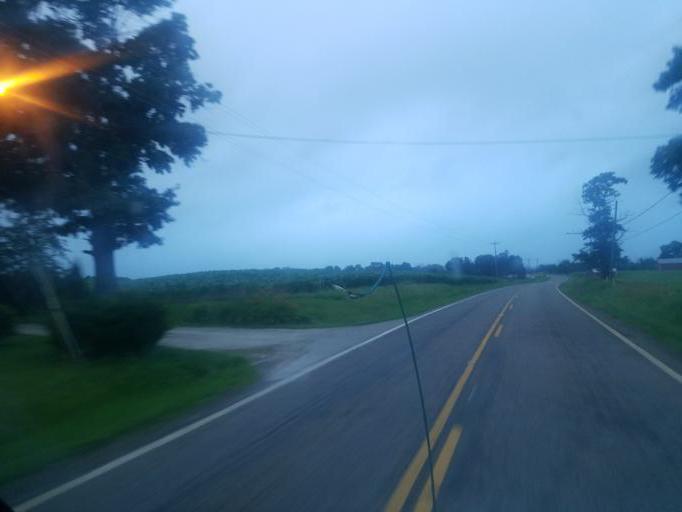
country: US
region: Ohio
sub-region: Columbiana County
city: Salineville
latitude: 40.6173
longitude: -80.9383
